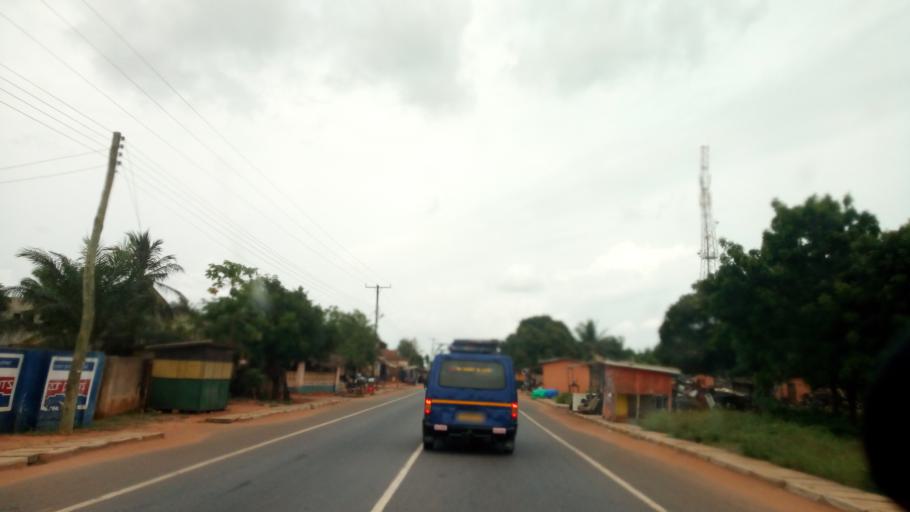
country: GH
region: Volta
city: Keta
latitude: 6.0643
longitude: 0.9141
